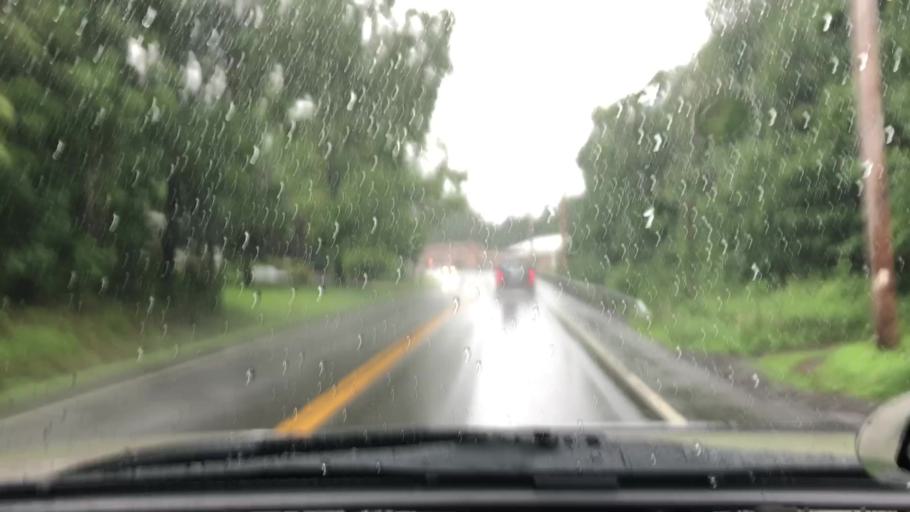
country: US
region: New York
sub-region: Greene County
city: Cairo
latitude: 42.2433
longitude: -73.9794
